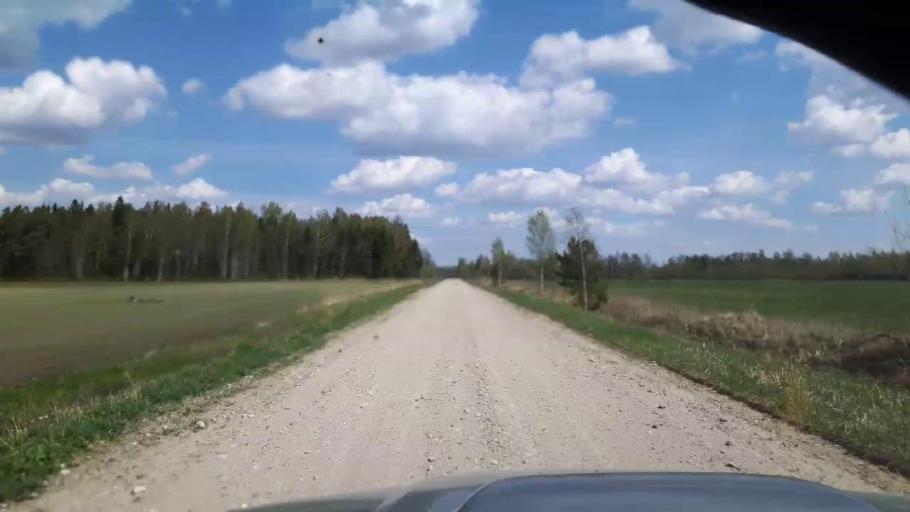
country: EE
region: Paernumaa
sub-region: Tootsi vald
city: Tootsi
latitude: 58.4656
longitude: 24.8912
